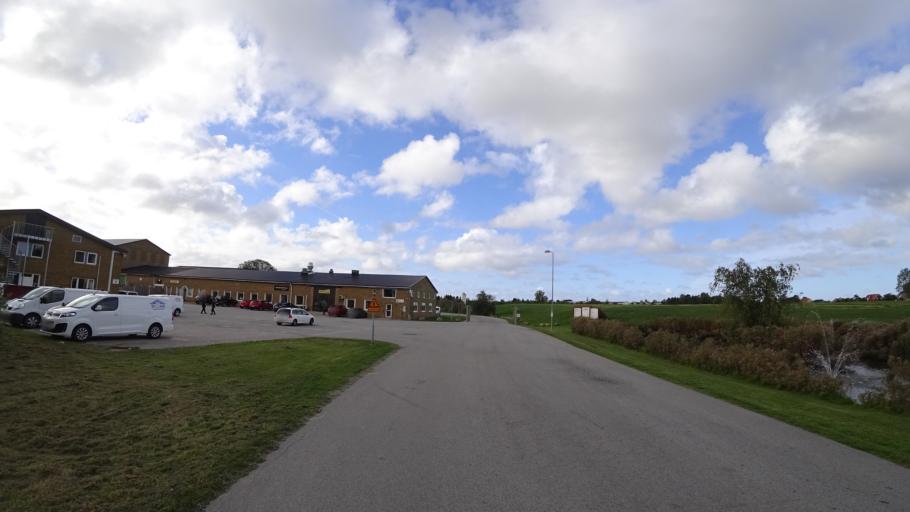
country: SE
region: Skane
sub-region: Kavlinge Kommun
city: Loddekopinge
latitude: 55.7658
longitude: 13.0535
